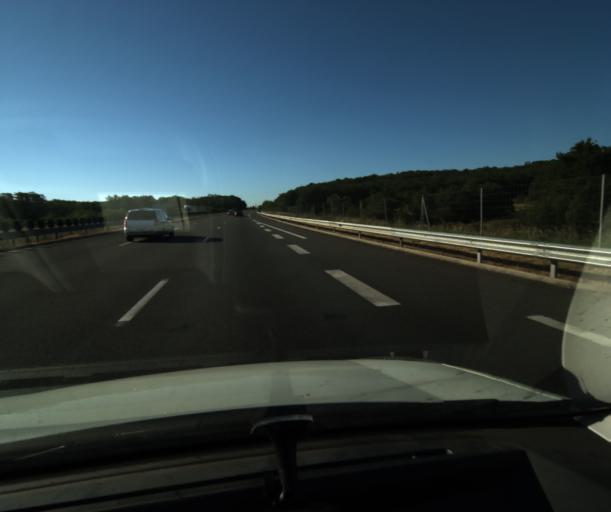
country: FR
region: Midi-Pyrenees
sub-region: Departement de la Haute-Garonne
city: Castelnau-d'Estretefonds
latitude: 43.8073
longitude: 1.3654
